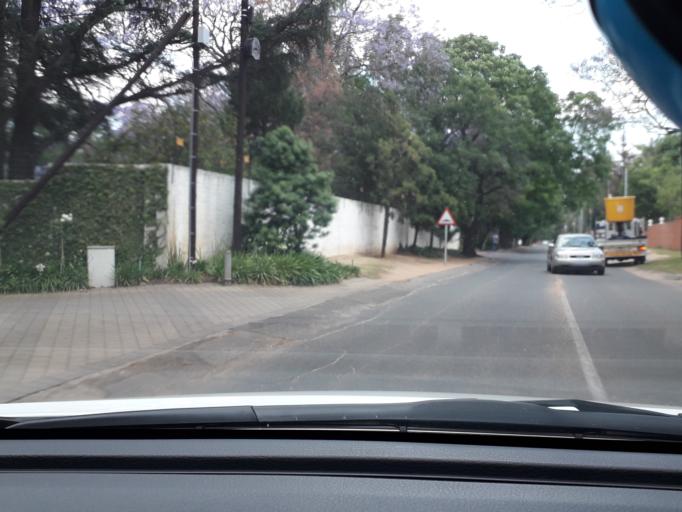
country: ZA
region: Gauteng
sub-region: City of Johannesburg Metropolitan Municipality
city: Johannesburg
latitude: -26.1106
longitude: 28.0638
